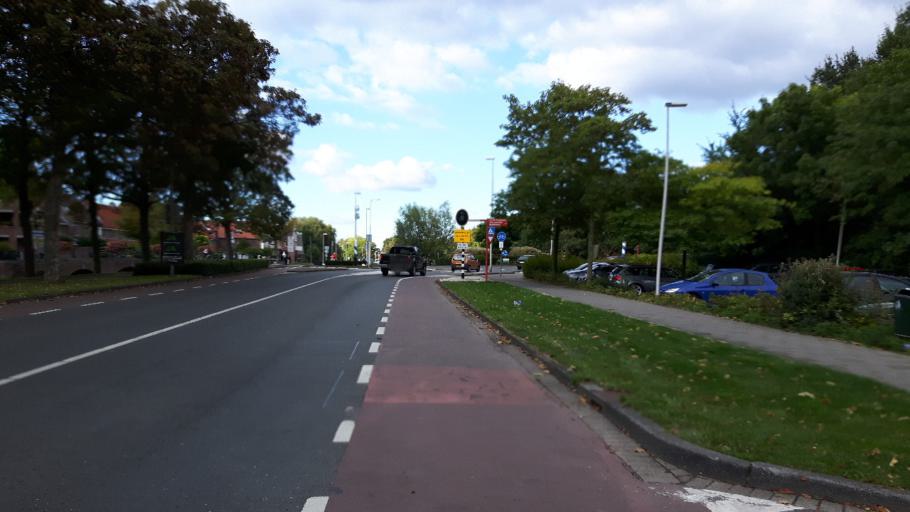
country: NL
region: Utrecht
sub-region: Gemeente Vianen
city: Vianen
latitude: 51.9921
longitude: 5.0963
